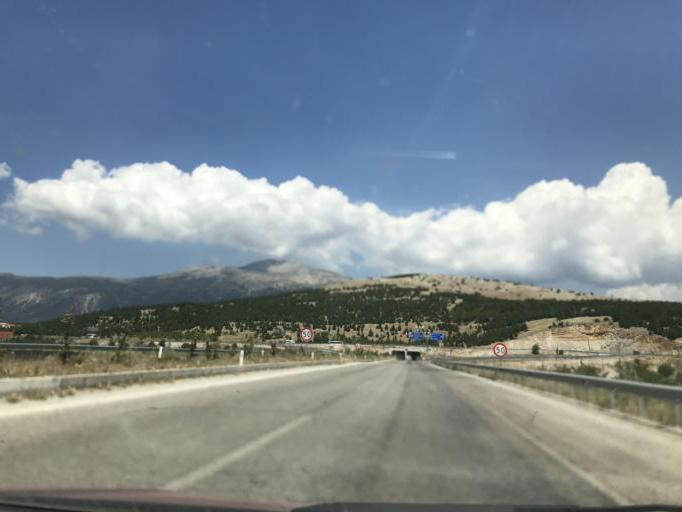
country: TR
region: Denizli
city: Serinhisar
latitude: 37.6283
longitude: 29.2135
